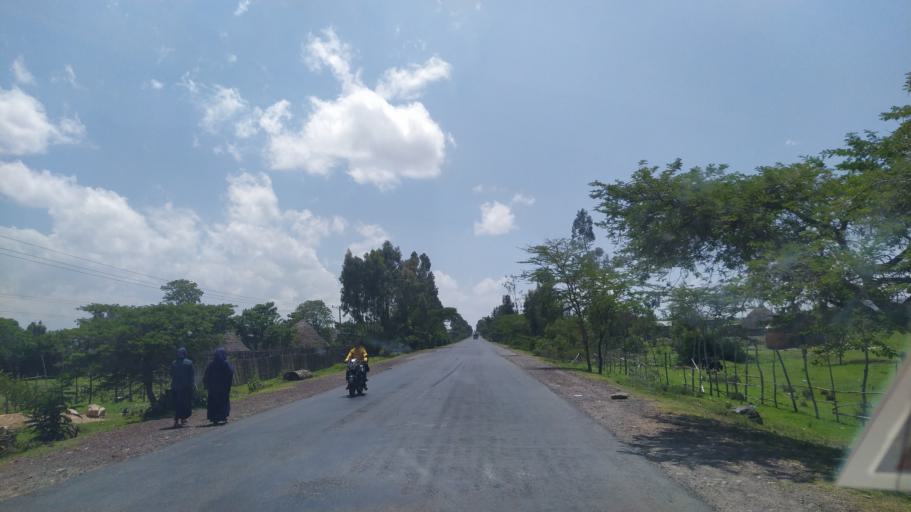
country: ET
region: Southern Nations, Nationalities, and People's Region
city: K'olito
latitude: 7.7490
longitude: 38.1271
